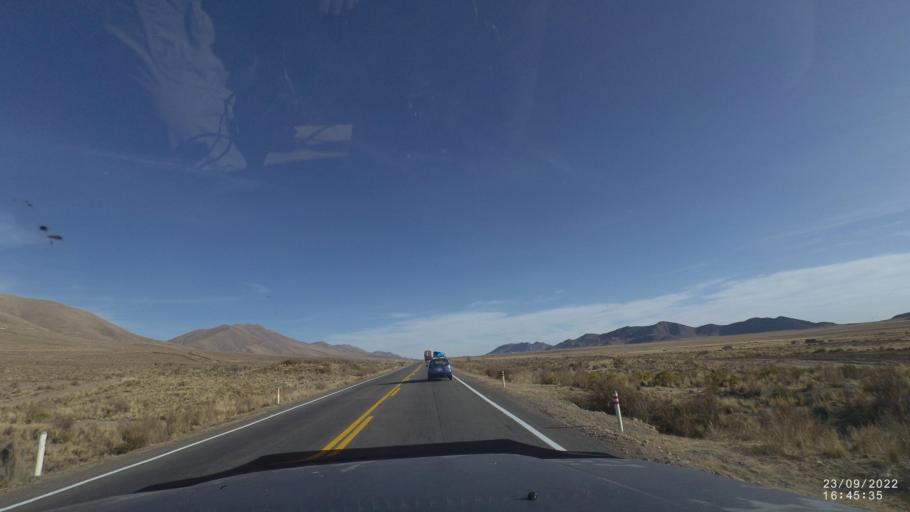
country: BO
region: Oruro
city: Poopo
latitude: -18.3437
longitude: -66.9856
